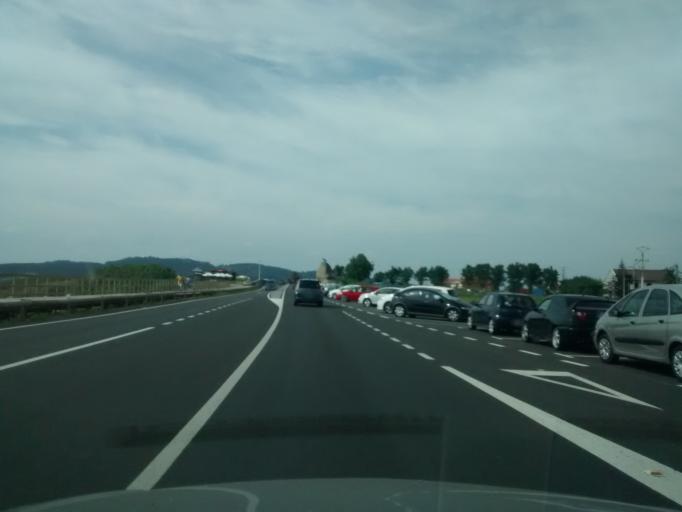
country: ES
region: Galicia
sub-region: Provincia de Pontevedra
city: O Grove
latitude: 42.4347
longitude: -8.8704
